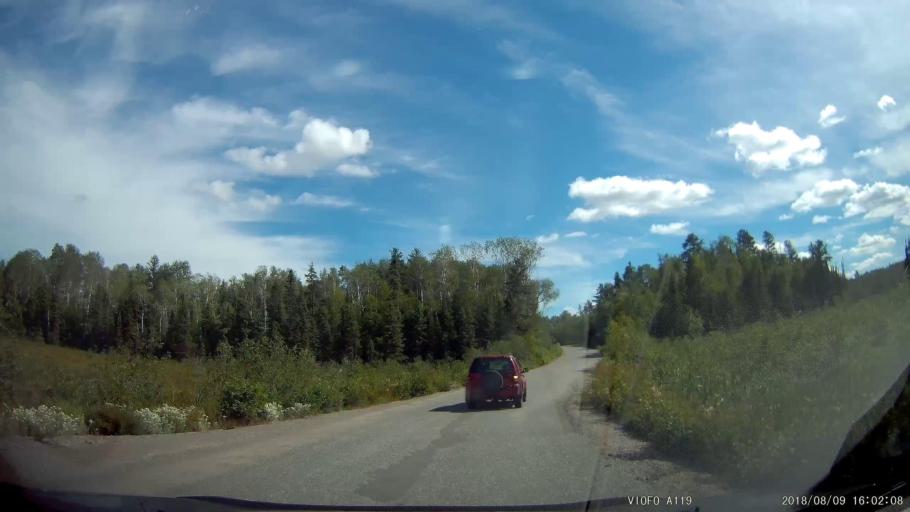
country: CA
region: Ontario
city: Rayside-Balfour
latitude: 46.6158
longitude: -81.4660
